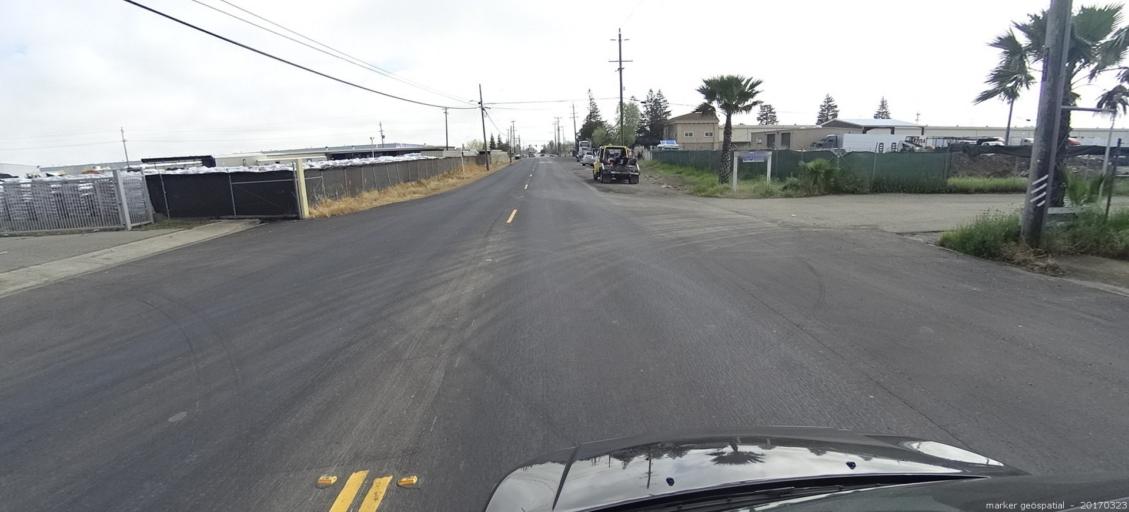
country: US
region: California
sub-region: Sacramento County
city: Florin
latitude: 38.5107
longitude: -121.3747
